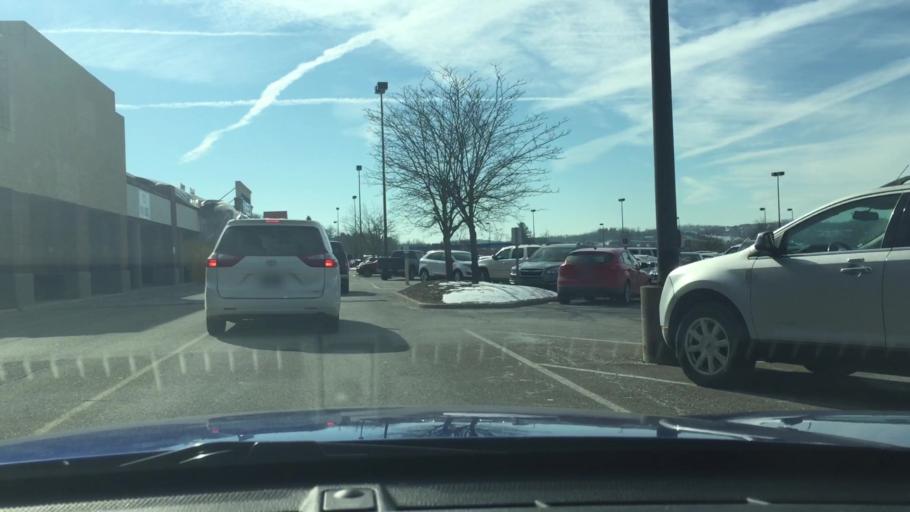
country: US
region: Pennsylvania
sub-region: Washington County
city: Thompsonville
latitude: 40.2710
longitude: -80.1264
